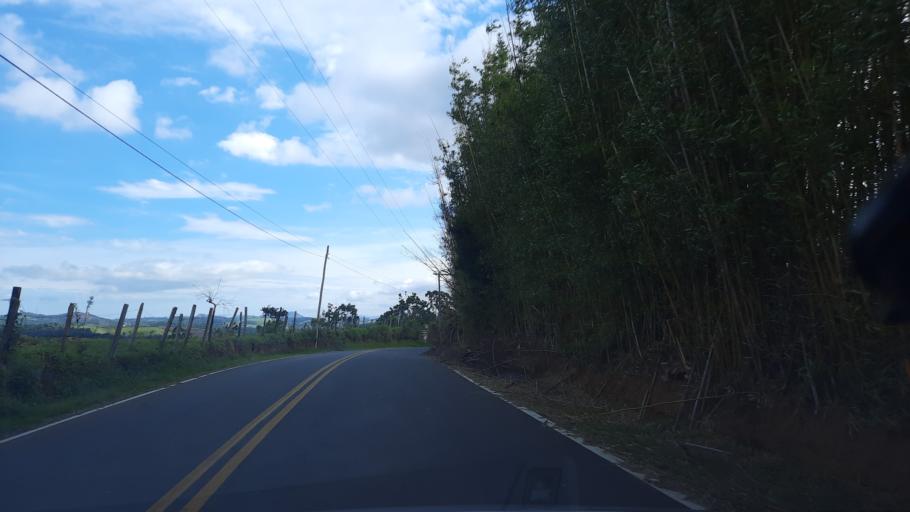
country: BR
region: Sao Paulo
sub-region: Atibaia
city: Atibaia
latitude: -23.0877
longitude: -46.5113
